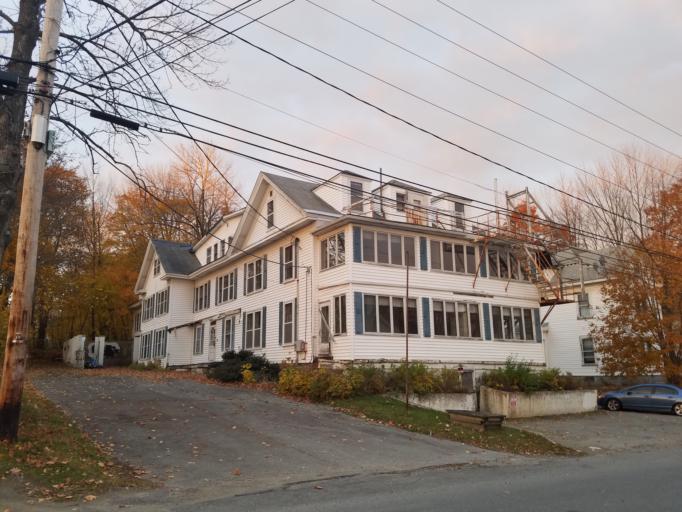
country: US
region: Maine
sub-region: Waldo County
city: Belfast
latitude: 44.4239
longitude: -69.0027
